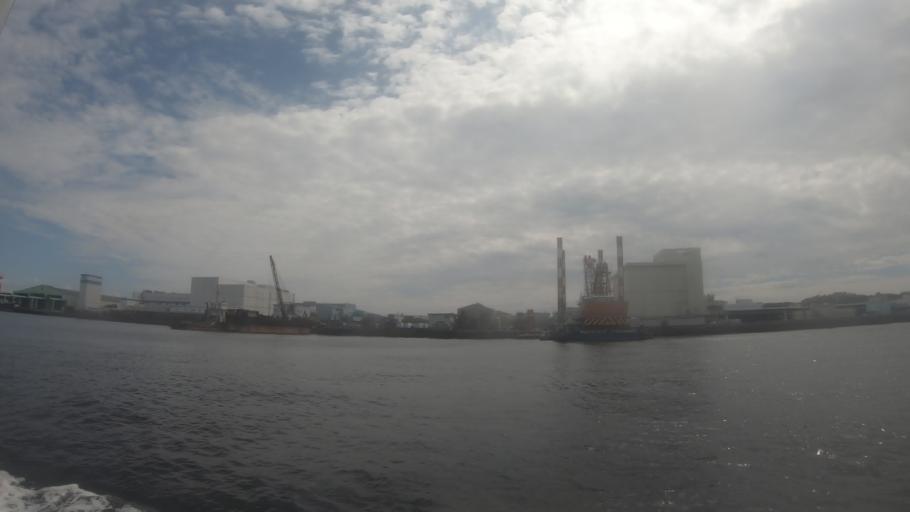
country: JP
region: Kanagawa
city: Yokohama
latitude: 35.3856
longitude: 139.6355
